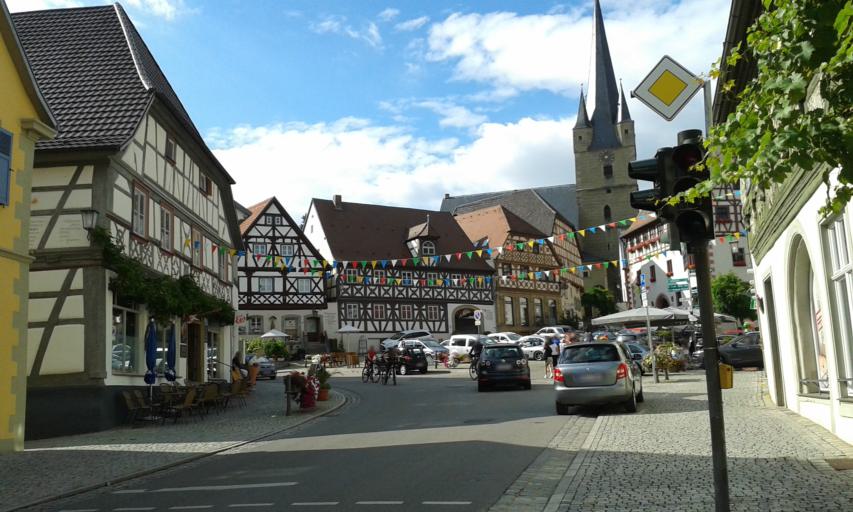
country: DE
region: Bavaria
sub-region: Regierungsbezirk Unterfranken
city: Zeil
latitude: 50.0094
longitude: 10.5949
